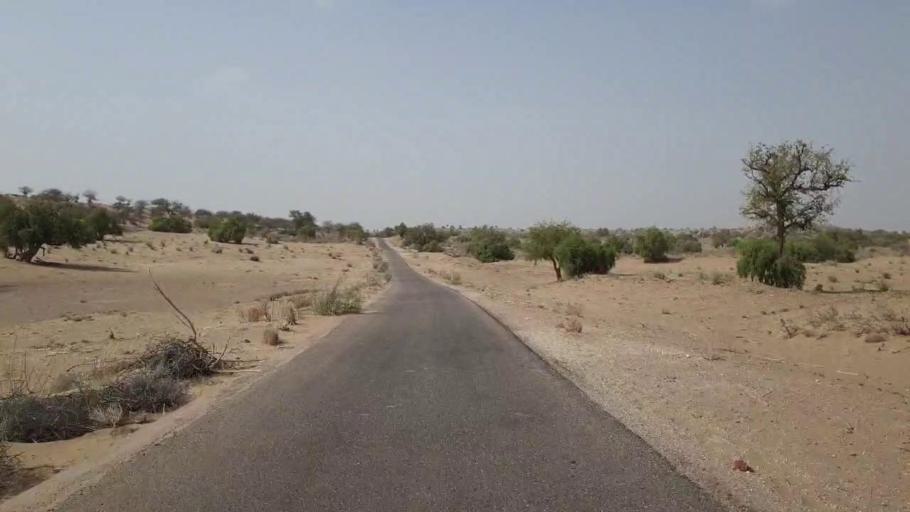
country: PK
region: Sindh
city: Mithi
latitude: 24.5905
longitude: 69.9236
